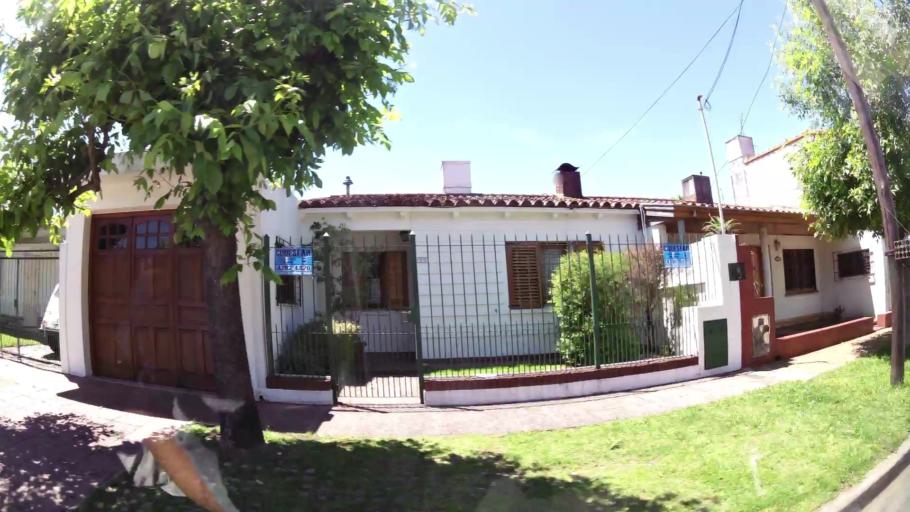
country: AR
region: Buenos Aires
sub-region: Partido de Quilmes
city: Quilmes
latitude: -34.7397
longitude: -58.2780
